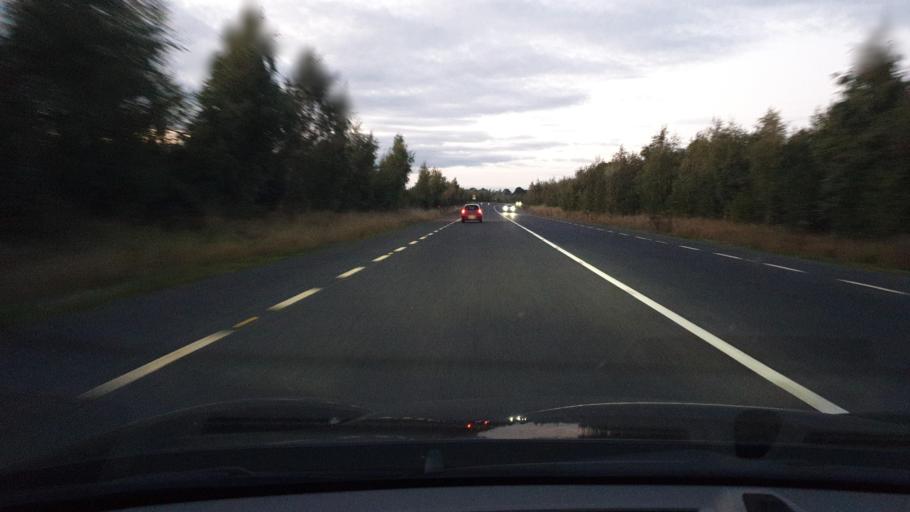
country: IE
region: Leinster
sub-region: An Mhi
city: Dunboyne
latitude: 53.4176
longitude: -6.4910
